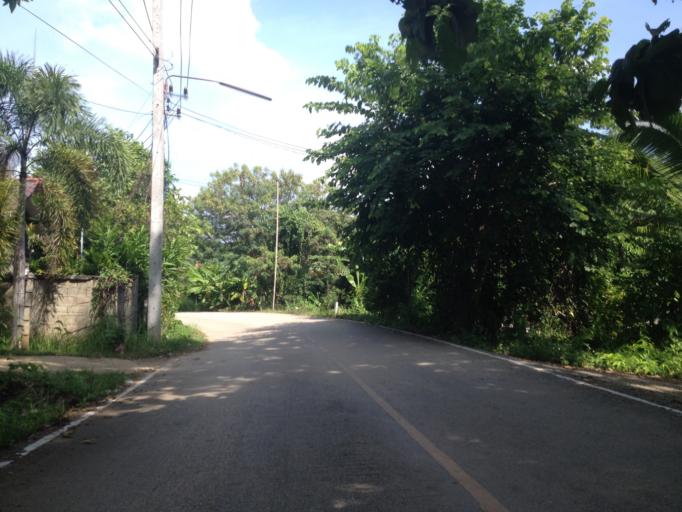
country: TH
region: Chiang Mai
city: Hang Dong
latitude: 18.7244
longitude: 98.9064
